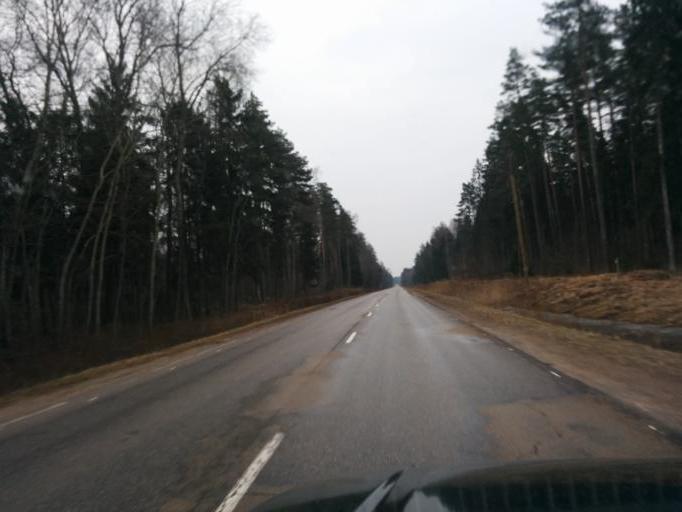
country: LV
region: Ikskile
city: Ikskile
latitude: 56.8147
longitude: 24.4739
